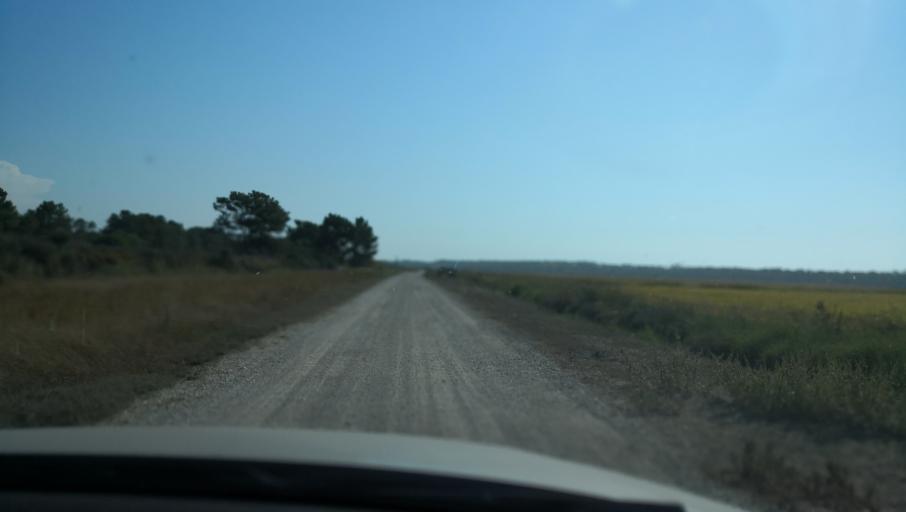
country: PT
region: Setubal
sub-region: Setubal
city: Setubal
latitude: 38.3945
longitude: -8.7886
